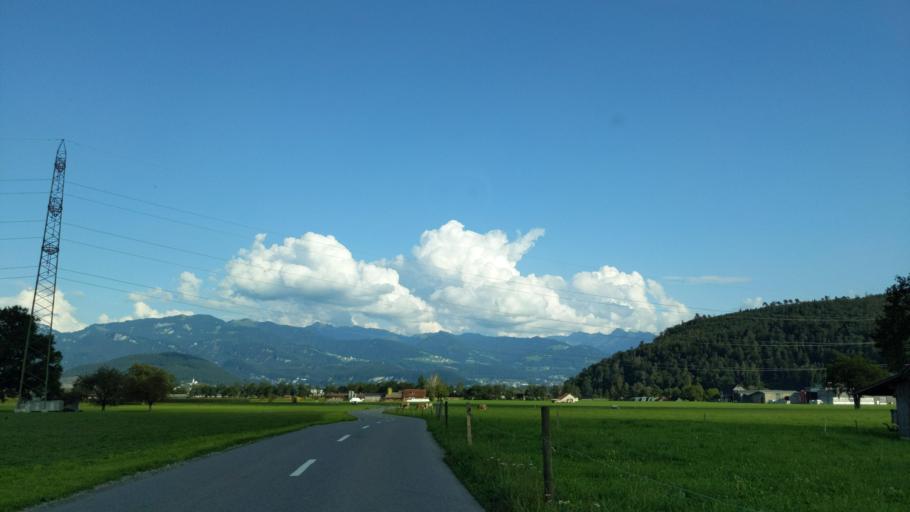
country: CH
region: Saint Gallen
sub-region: Wahlkreis Rheintal
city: Eichberg
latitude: 47.3361
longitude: 9.5388
